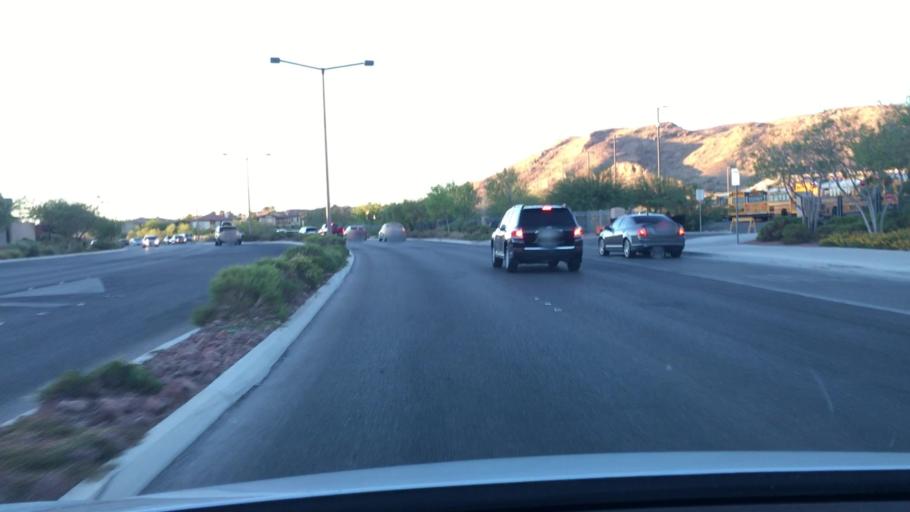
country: US
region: Nevada
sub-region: Clark County
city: Summerlin South
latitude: 36.1584
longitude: -115.3522
